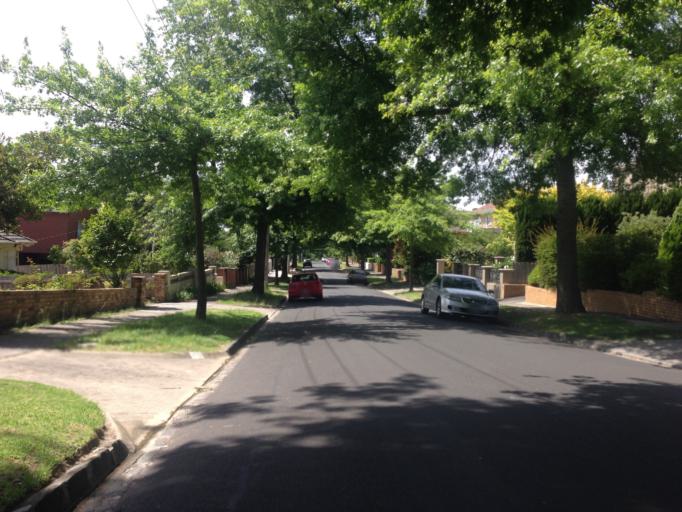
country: AU
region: Victoria
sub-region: Boroondara
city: Balwyn North
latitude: -37.7923
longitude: 145.0747
